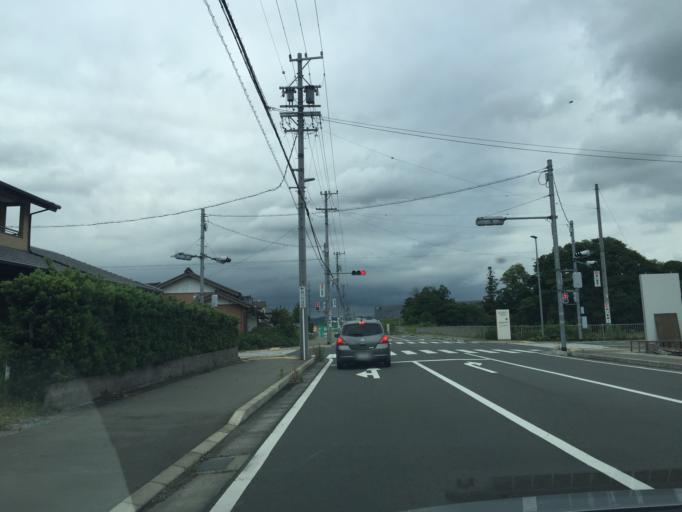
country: JP
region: Shizuoka
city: Kakegawa
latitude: 34.7571
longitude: 137.9945
